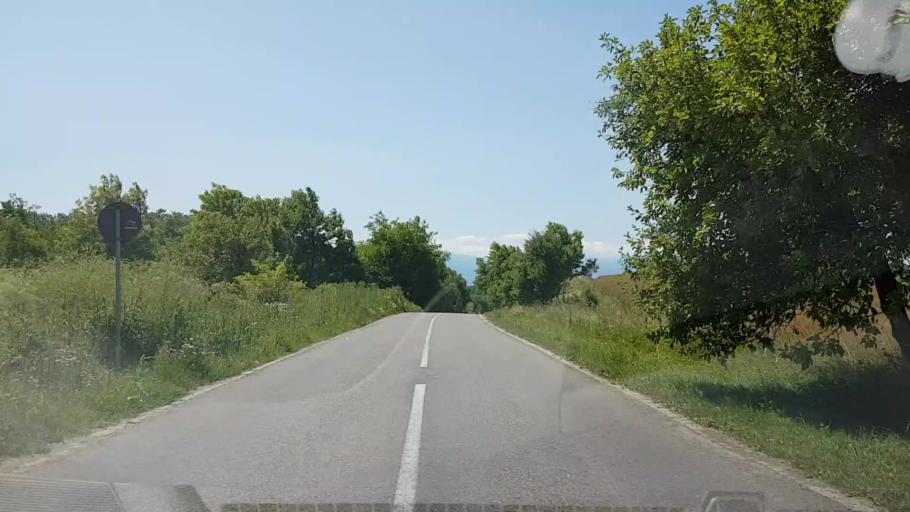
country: RO
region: Brasov
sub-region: Comuna Cincu
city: Cincu
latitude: 45.8985
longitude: 24.8121
